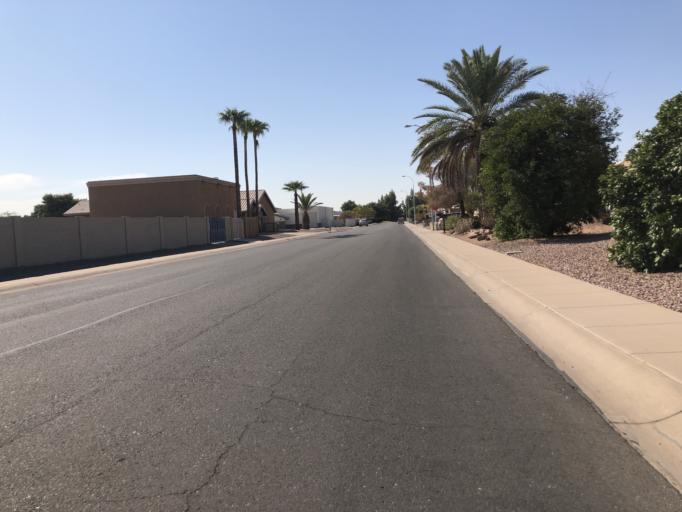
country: US
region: Arizona
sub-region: Maricopa County
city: Chandler
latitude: 33.3009
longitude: -111.9188
